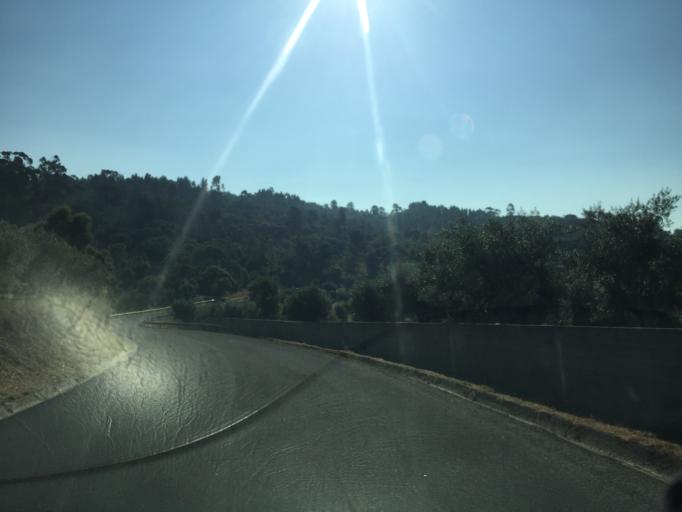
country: PT
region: Santarem
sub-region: Abrantes
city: Alferrarede
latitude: 39.5228
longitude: -8.1497
